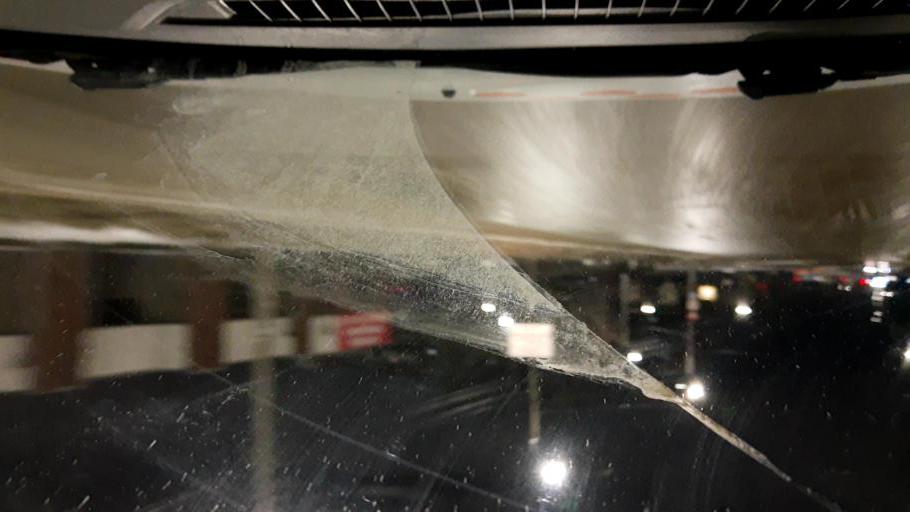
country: RU
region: Nizjnij Novgorod
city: Dzerzhinsk
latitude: 56.2299
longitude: 43.4570
